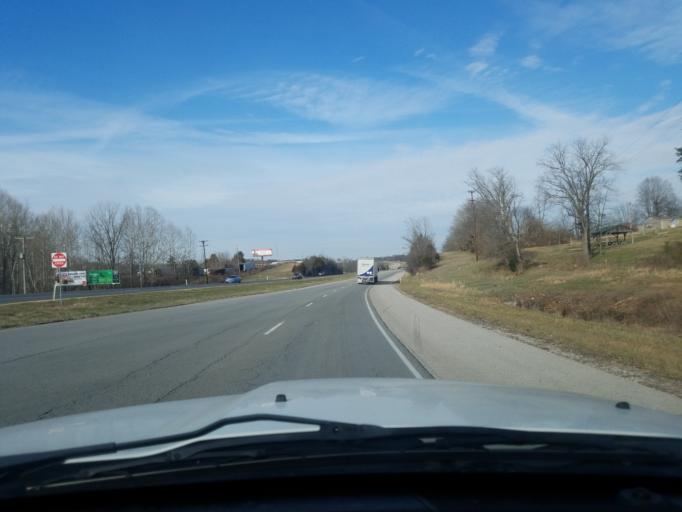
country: US
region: Indiana
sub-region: Monroe County
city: Bloomington
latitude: 39.0886
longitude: -86.5450
